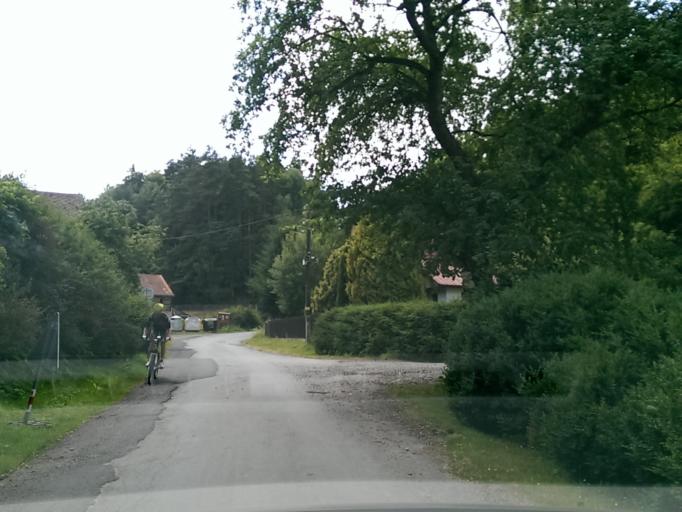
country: CZ
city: Duba
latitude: 50.4721
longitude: 14.5302
